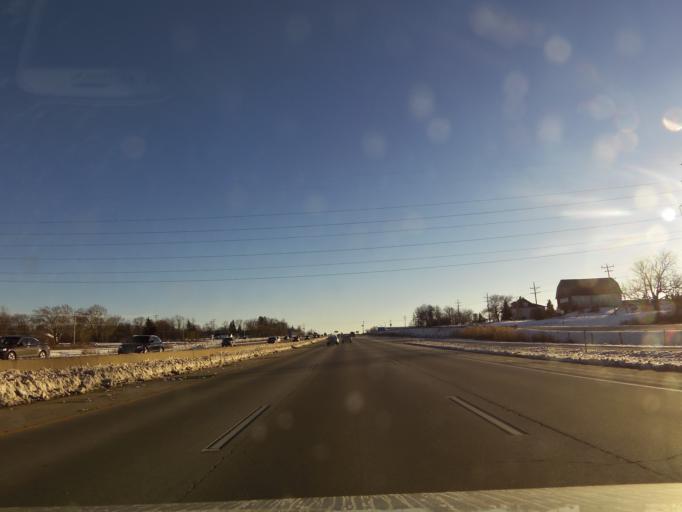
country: US
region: Wisconsin
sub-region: Racine County
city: Caledonia
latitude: 42.8270
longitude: -87.9529
